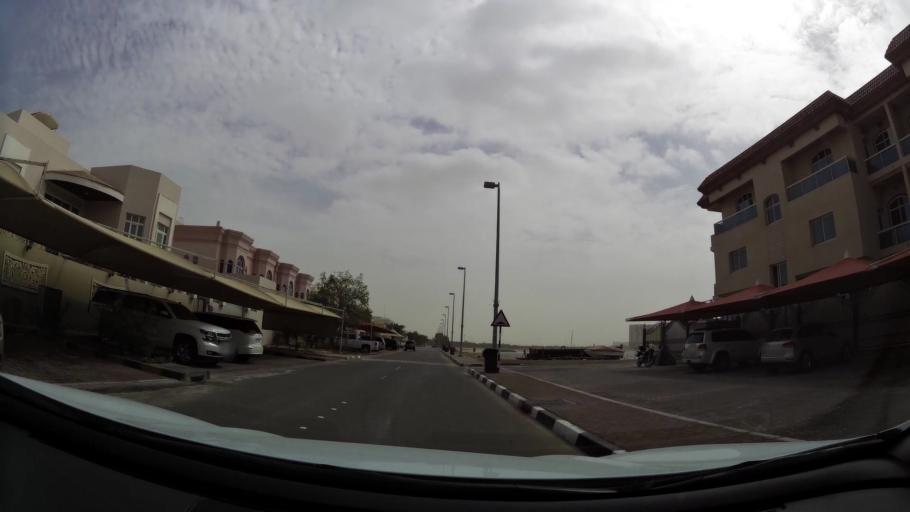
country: AE
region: Abu Dhabi
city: Abu Dhabi
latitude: 24.3929
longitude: 54.5133
